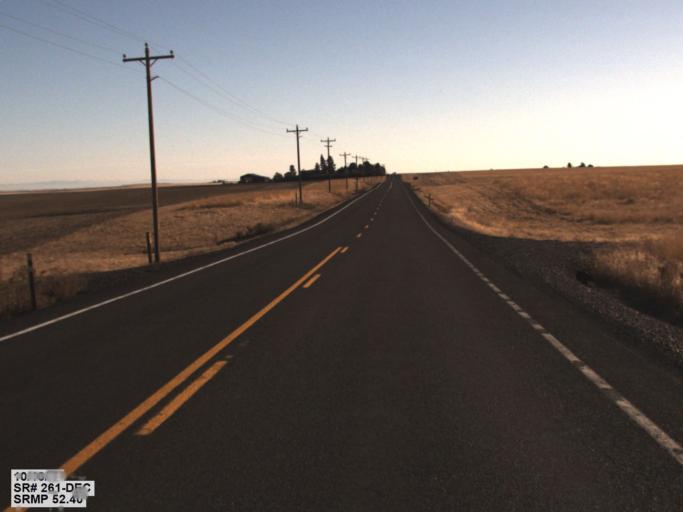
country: US
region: Washington
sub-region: Adams County
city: Ritzville
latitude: 46.9720
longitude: -118.3434
